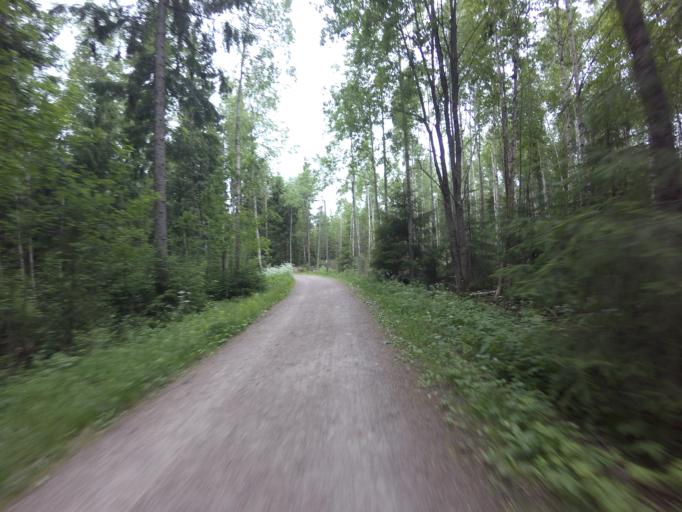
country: FI
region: Uusimaa
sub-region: Helsinki
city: Kauniainen
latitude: 60.1847
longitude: 24.7105
